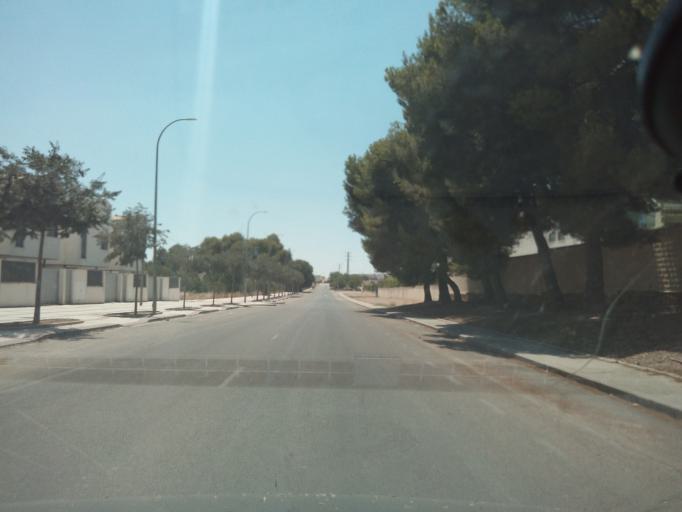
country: ES
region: Castille-La Mancha
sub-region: Province of Toledo
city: Villacanas
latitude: 39.6143
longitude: -3.3418
